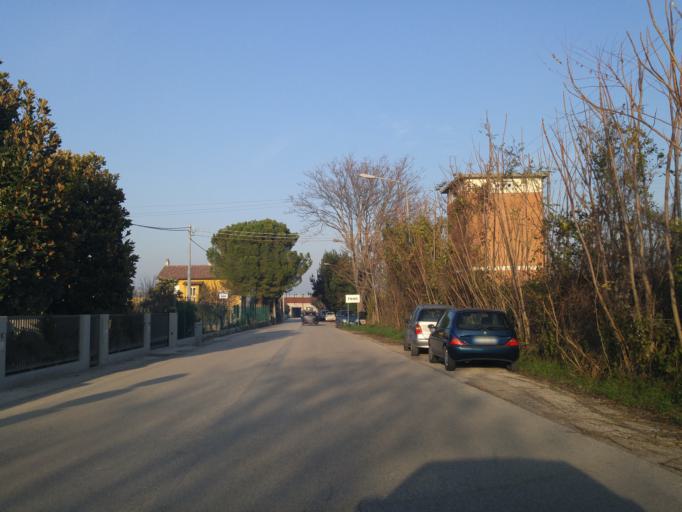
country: IT
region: The Marches
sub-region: Provincia di Pesaro e Urbino
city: Rosciano
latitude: 43.8184
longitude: 13.0010
